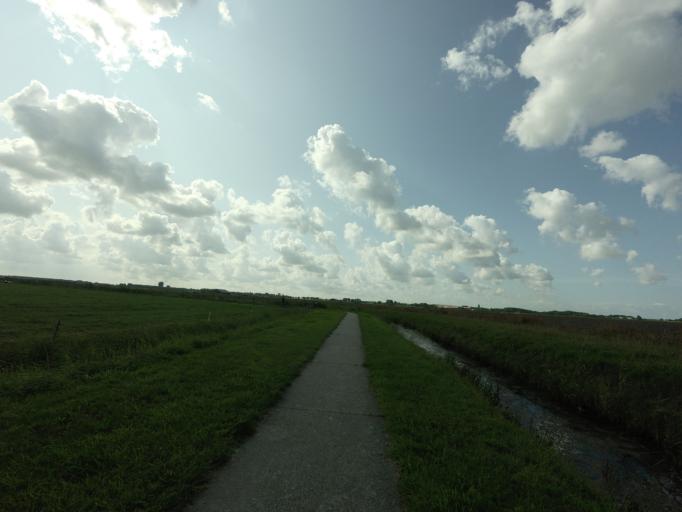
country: NL
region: Friesland
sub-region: Gemeente Het Bildt
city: Sint Jacobiparochie
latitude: 53.2687
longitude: 5.6092
